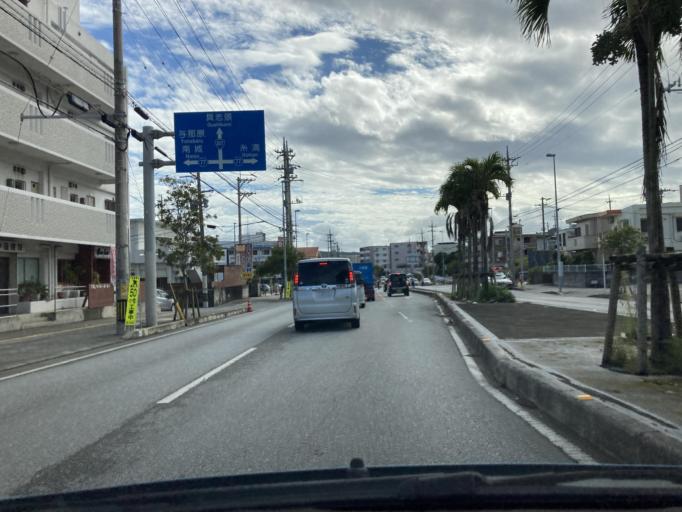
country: JP
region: Okinawa
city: Tomigusuku
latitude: 26.1559
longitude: 127.7213
